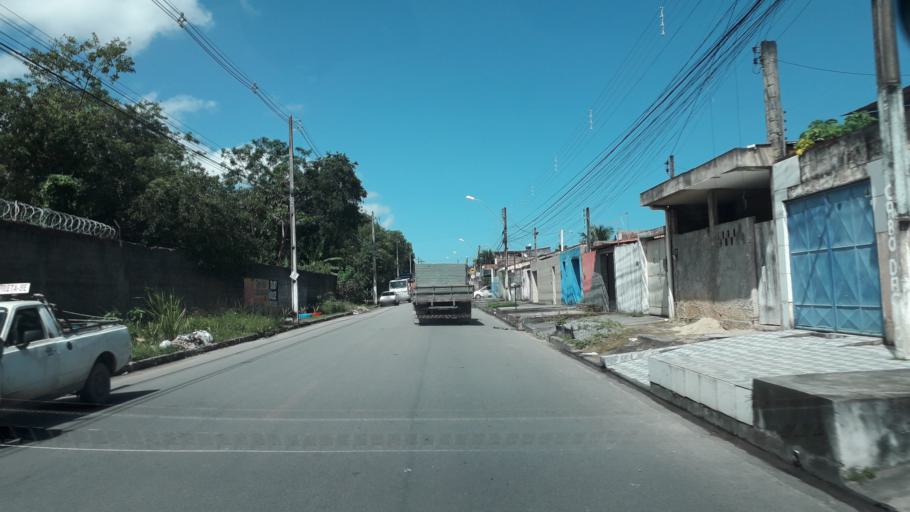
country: BR
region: Alagoas
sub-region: Satuba
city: Satuba
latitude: -9.5586
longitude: -35.7833
